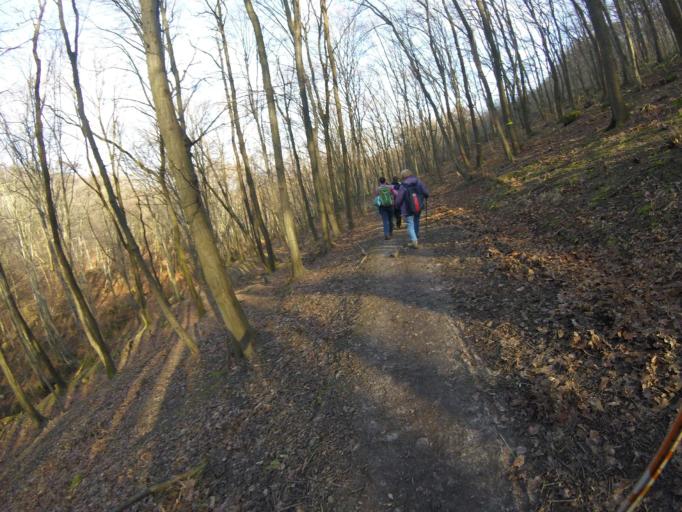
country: HU
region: Komarom-Esztergom
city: Pilismarot
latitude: 47.7548
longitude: 18.8923
